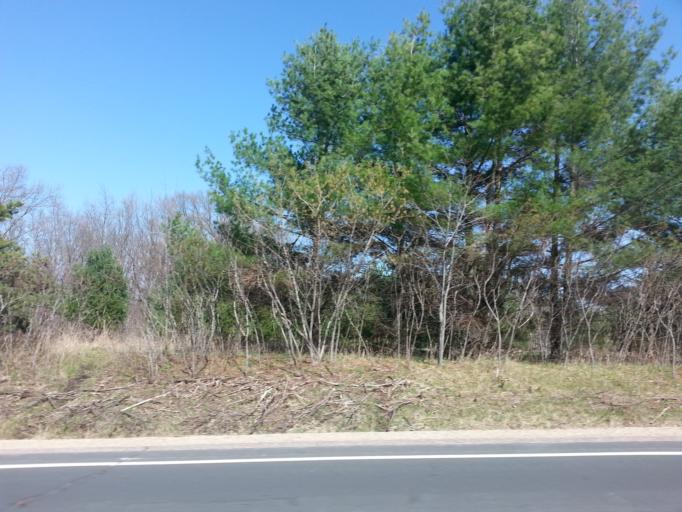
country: US
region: Wisconsin
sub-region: Dunn County
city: Menomonie
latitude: 44.7579
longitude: -91.9329
